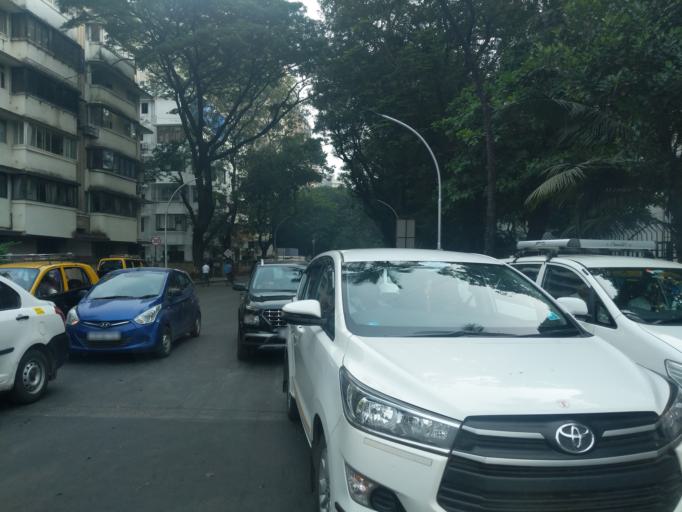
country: IN
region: Maharashtra
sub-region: Raigarh
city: Uran
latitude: 18.9261
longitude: 72.8269
